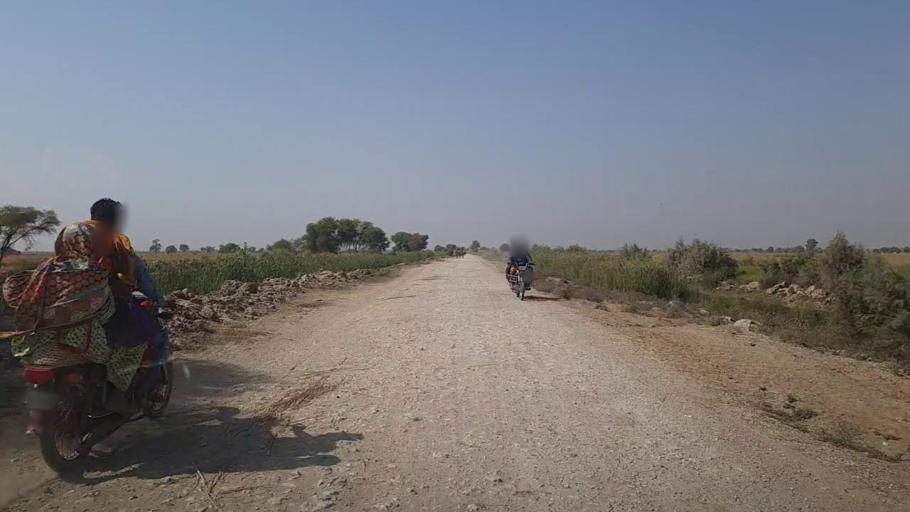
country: PK
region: Sindh
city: Kandhkot
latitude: 28.3978
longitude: 69.2692
